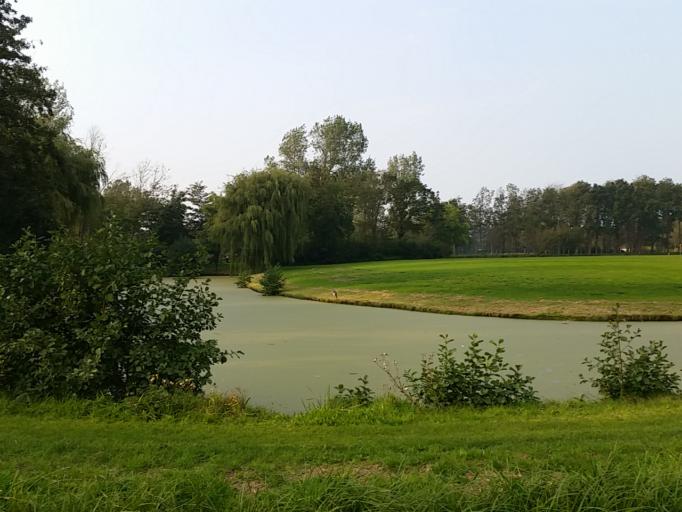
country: NL
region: South Holland
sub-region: Gemeente Noordwijk
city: Noordwijk-Binnen
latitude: 52.2174
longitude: 4.4286
